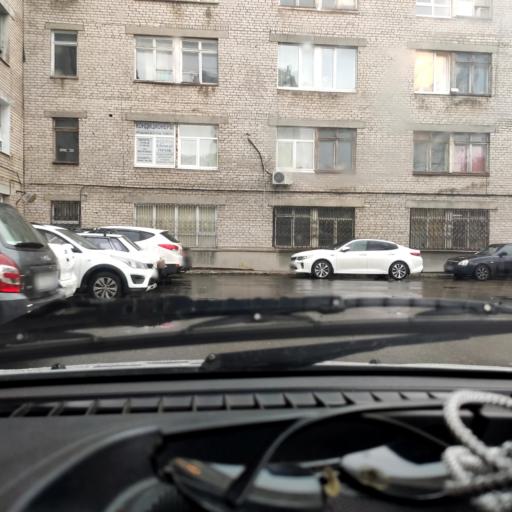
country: RU
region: Samara
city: Zhigulevsk
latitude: 53.4799
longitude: 49.4871
